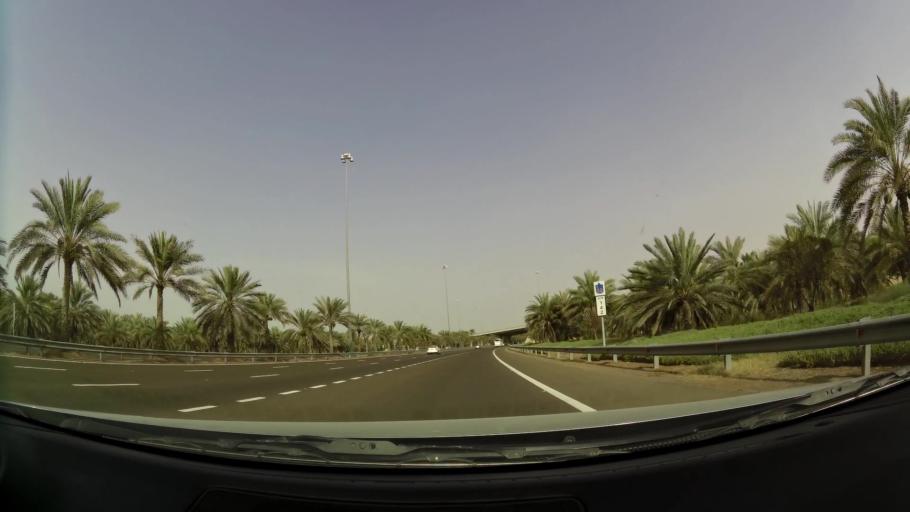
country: AE
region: Abu Dhabi
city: Al Ain
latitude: 24.2010
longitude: 55.5821
